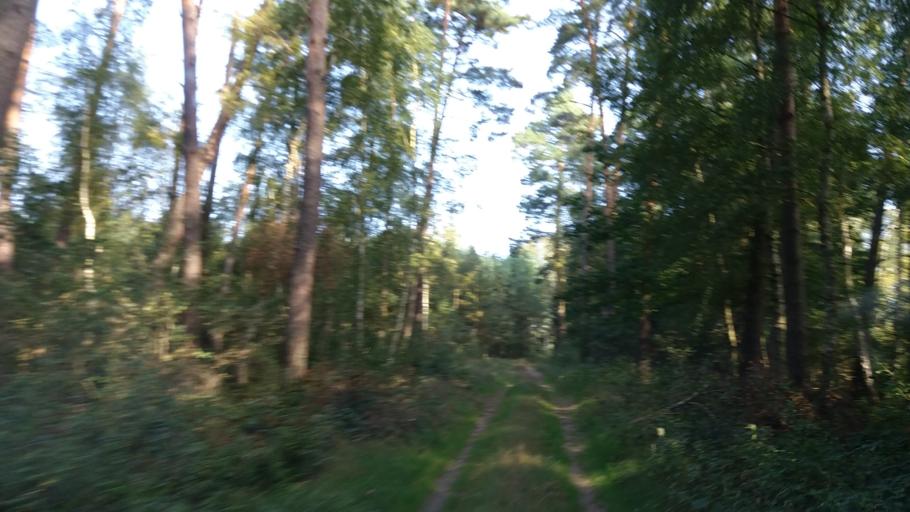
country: PL
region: West Pomeranian Voivodeship
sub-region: Powiat stargardzki
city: Suchan
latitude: 53.2466
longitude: 15.3662
